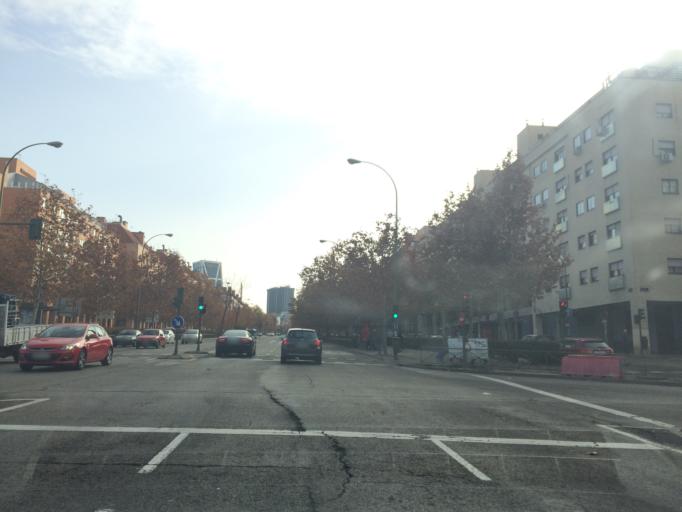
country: ES
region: Madrid
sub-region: Provincia de Madrid
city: Tetuan de las Victorias
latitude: 40.4722
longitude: -3.6996
